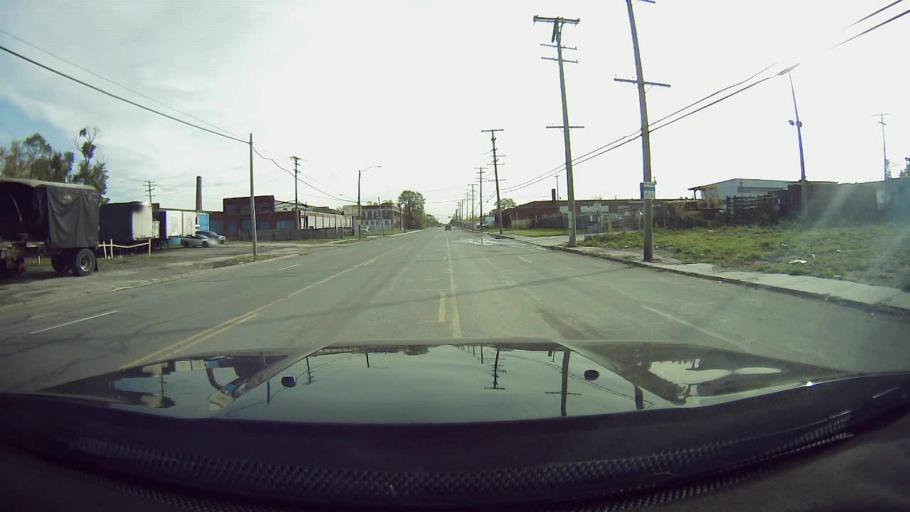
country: US
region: Michigan
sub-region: Wayne County
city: Hamtramck
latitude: 42.4194
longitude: -83.0309
